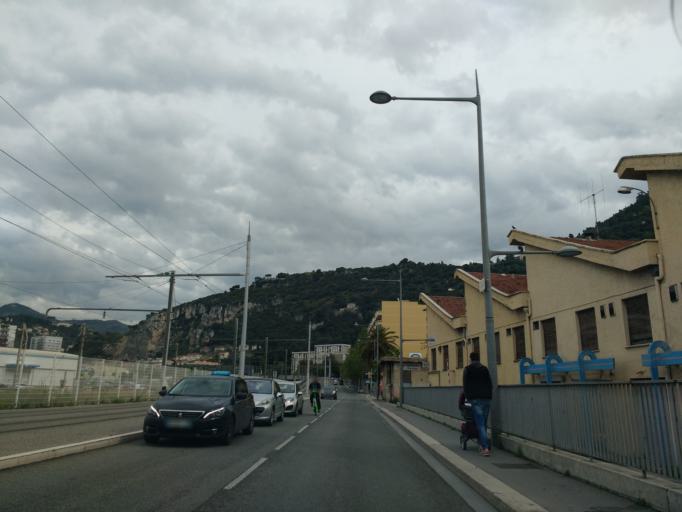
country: FR
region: Provence-Alpes-Cote d'Azur
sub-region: Departement des Alpes-Maritimes
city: Saint-Andre-de-la-Roche
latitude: 43.7196
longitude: 7.2917
